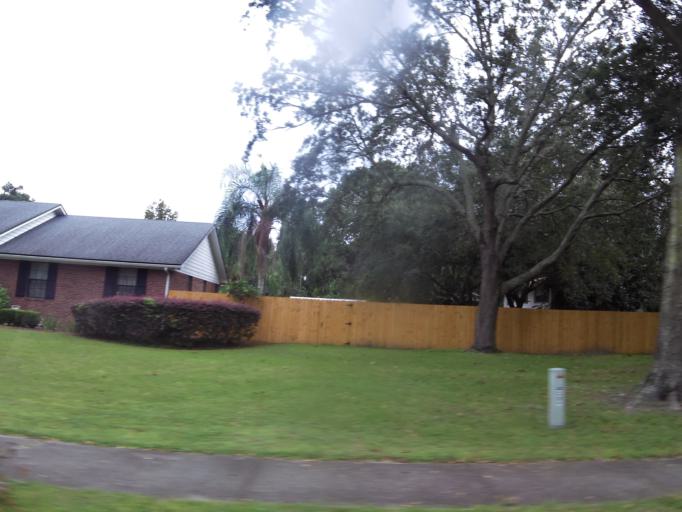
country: US
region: Florida
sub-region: Clay County
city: Bellair-Meadowbrook Terrace
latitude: 30.2584
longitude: -81.7260
